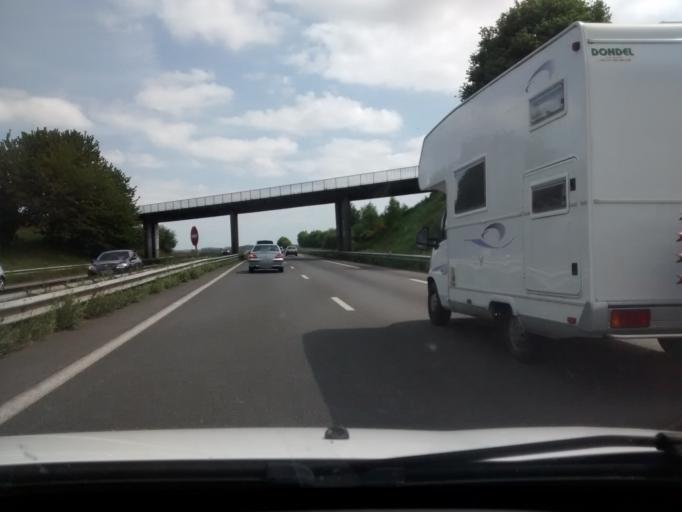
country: FR
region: Brittany
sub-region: Departement des Cotes-d'Armor
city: Plestan
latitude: 48.4454
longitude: -2.4802
